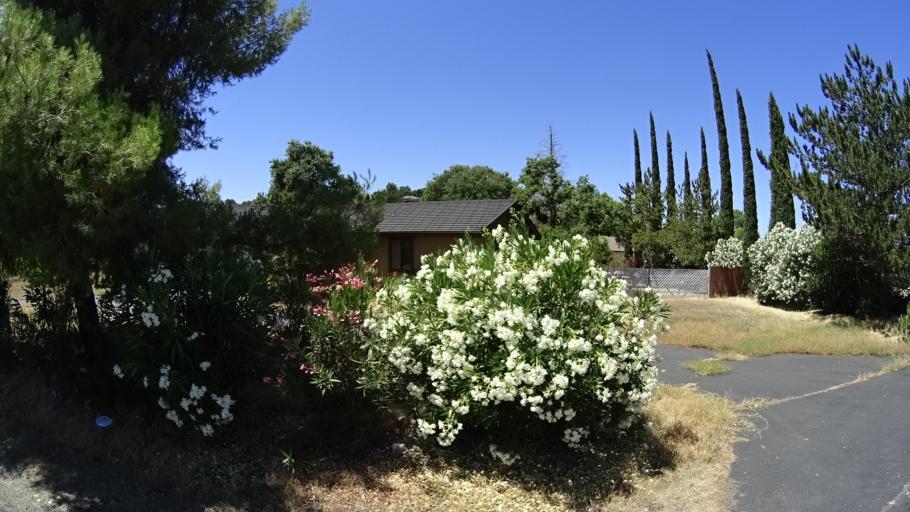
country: US
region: California
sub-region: Calaveras County
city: Valley Springs
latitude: 38.1673
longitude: -120.8371
